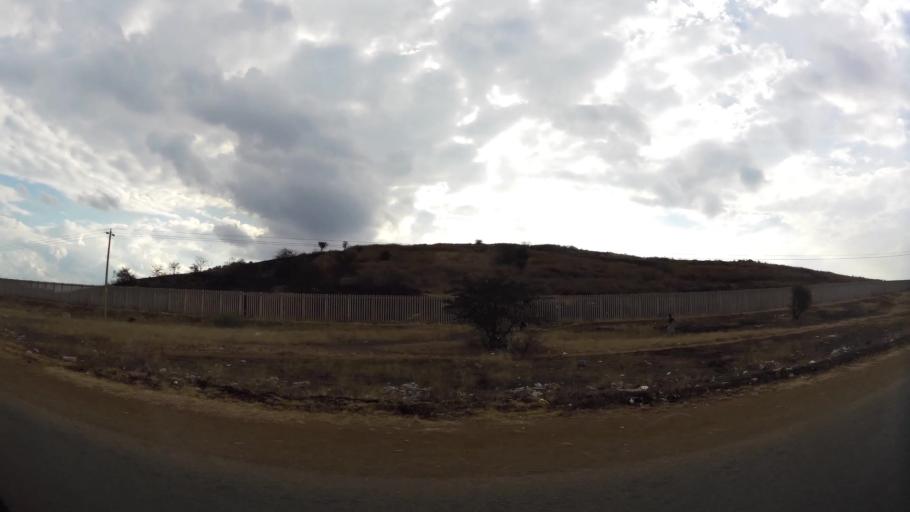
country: ZA
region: Gauteng
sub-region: Sedibeng District Municipality
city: Vanderbijlpark
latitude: -26.6699
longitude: 27.8618
